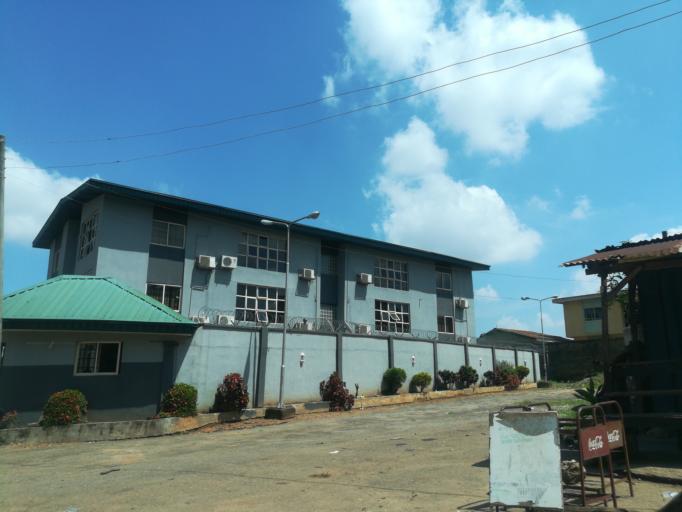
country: NG
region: Oyo
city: Ibadan
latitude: 7.3522
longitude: 3.8638
